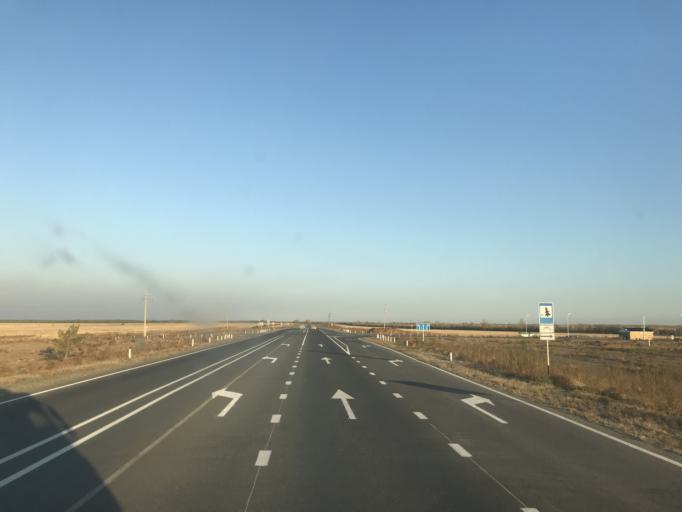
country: KZ
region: Pavlodar
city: Kurchatov
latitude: 50.9612
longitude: 79.3359
